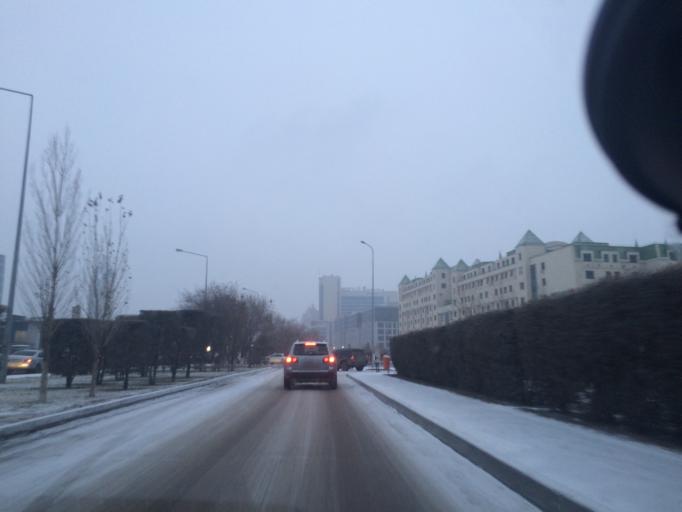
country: KZ
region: Astana Qalasy
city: Astana
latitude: 51.1388
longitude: 71.4169
